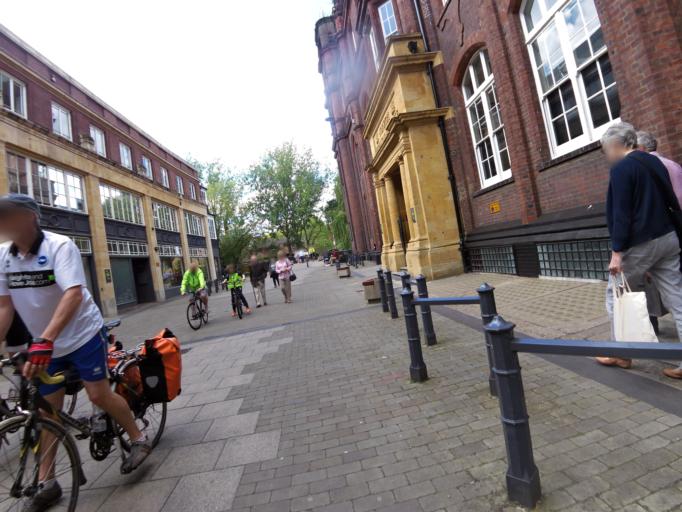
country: GB
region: England
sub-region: Norfolk
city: Norwich
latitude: 52.6315
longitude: 1.2951
